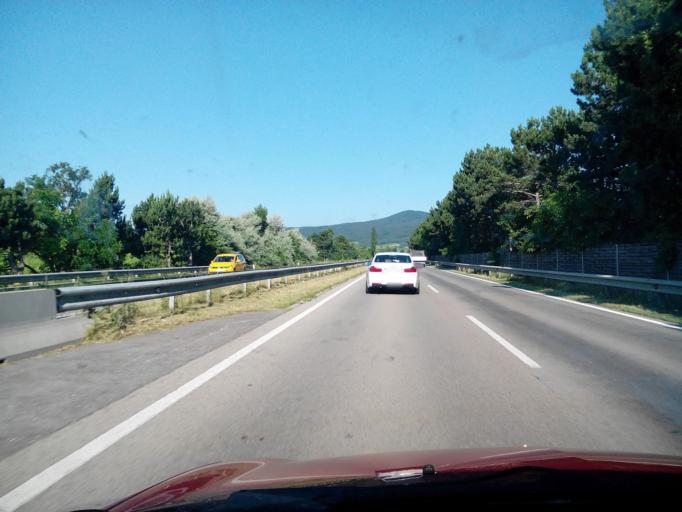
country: AT
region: Lower Austria
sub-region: Politischer Bezirk Baden
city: Baden
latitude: 47.9943
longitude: 16.2450
